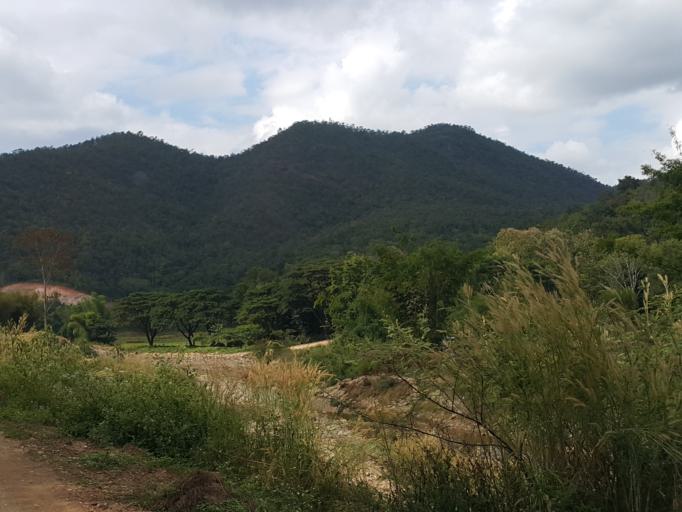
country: TH
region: Lampang
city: Chae Hom
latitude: 18.5723
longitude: 99.4452
